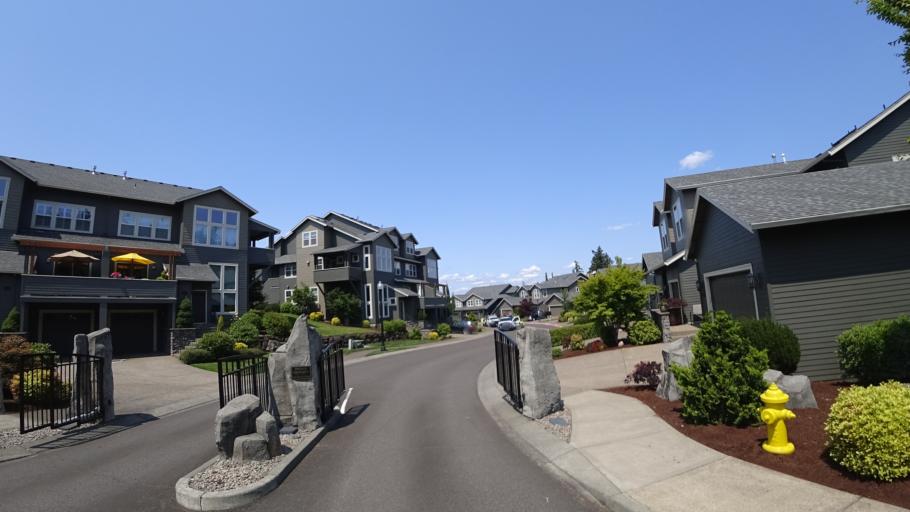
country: US
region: Oregon
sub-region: Multnomah County
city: Lents
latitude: 45.4584
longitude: -122.5568
